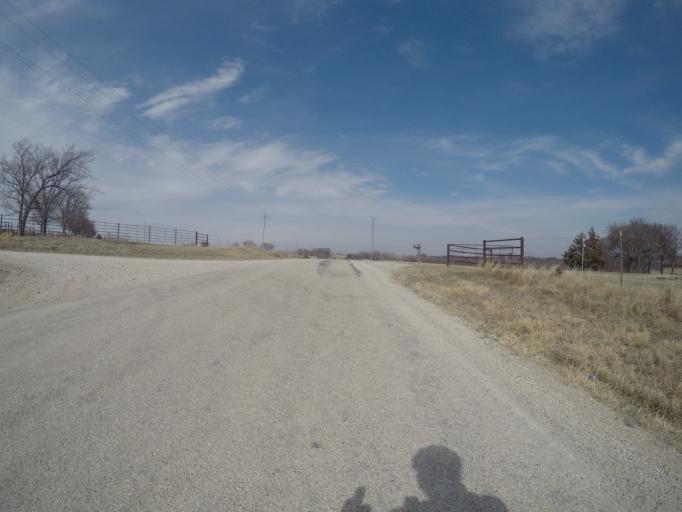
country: US
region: Kansas
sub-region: Geary County
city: Grandview Plaza
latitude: 39.0501
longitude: -96.7431
